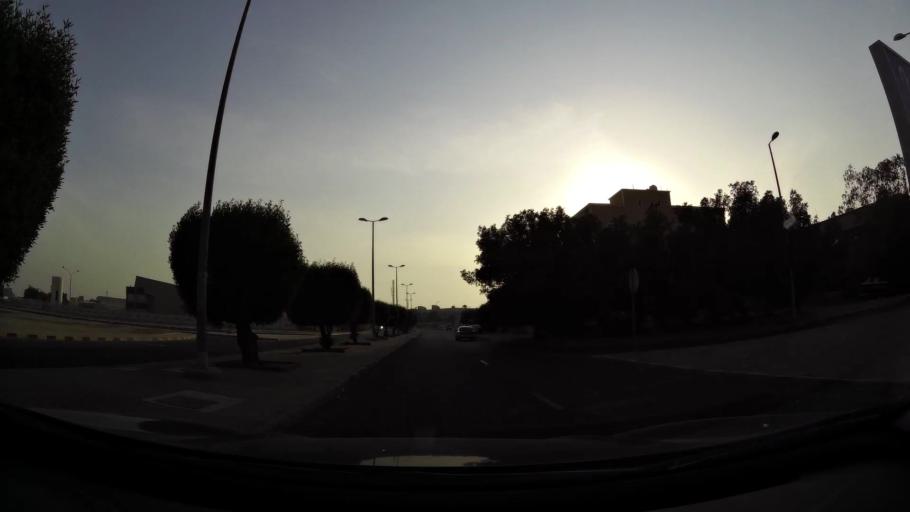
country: KW
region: Mubarak al Kabir
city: Sabah as Salim
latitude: 29.2452
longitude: 48.0624
